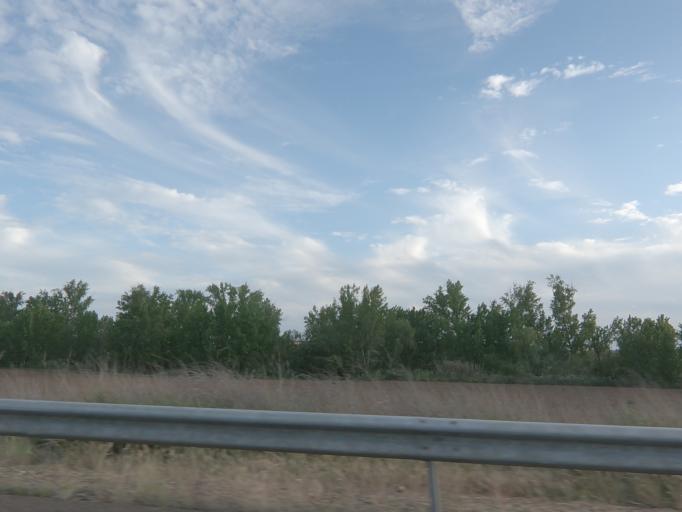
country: ES
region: Extremadura
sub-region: Provincia de Badajoz
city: Valdelacalzada
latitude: 38.8494
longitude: -6.6853
